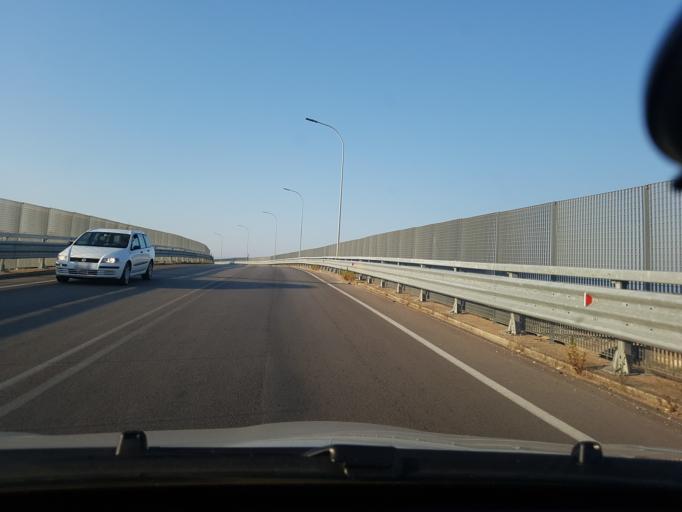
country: IT
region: Apulia
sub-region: Provincia di Foggia
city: Carapelle
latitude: 41.4055
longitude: 15.6524
